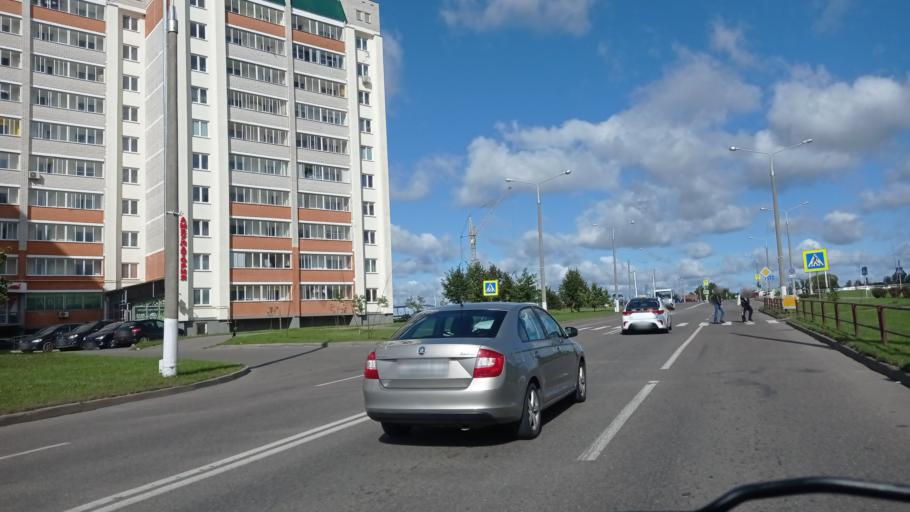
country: BY
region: Vitebsk
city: Vitebsk
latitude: 55.1722
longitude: 30.2579
